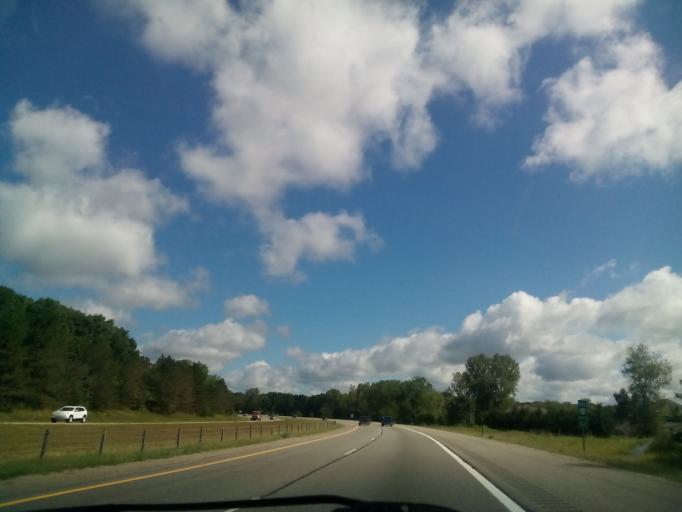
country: US
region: Michigan
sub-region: Livingston County
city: Brighton
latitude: 42.5578
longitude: -83.7424
